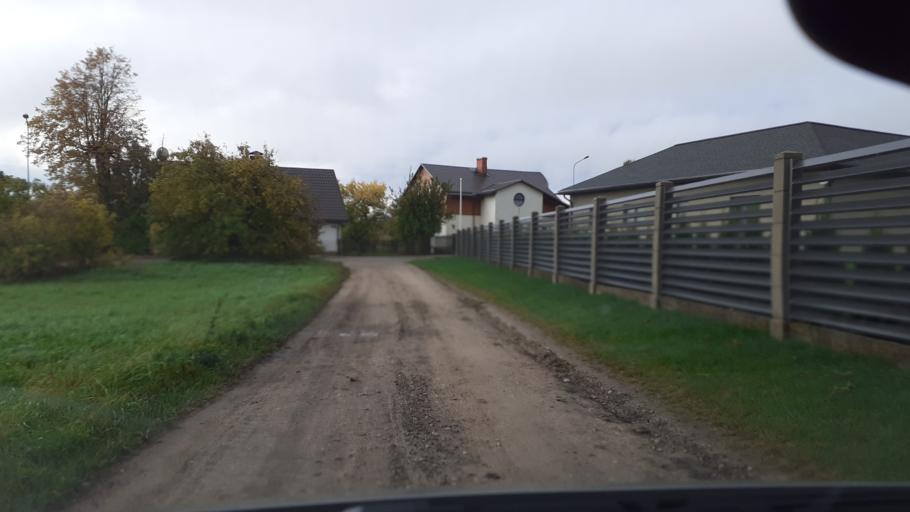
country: LV
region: Kuldigas Rajons
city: Kuldiga
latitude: 56.9712
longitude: 21.9388
